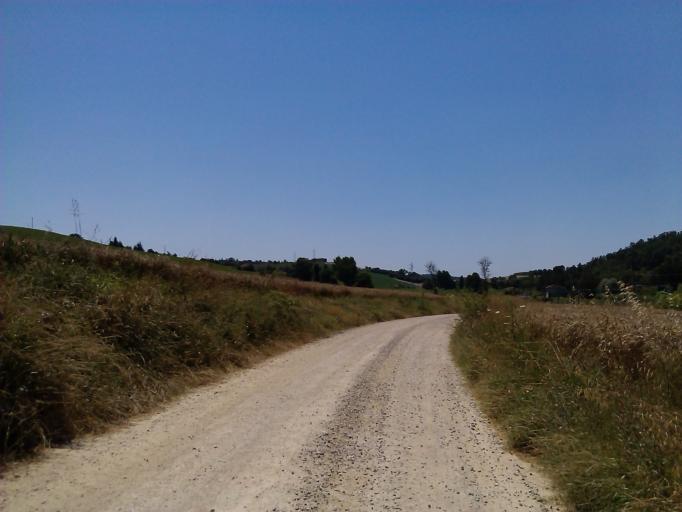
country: IT
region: Umbria
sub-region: Provincia di Terni
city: Fabro Scalo
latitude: 42.8501
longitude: 12.0408
